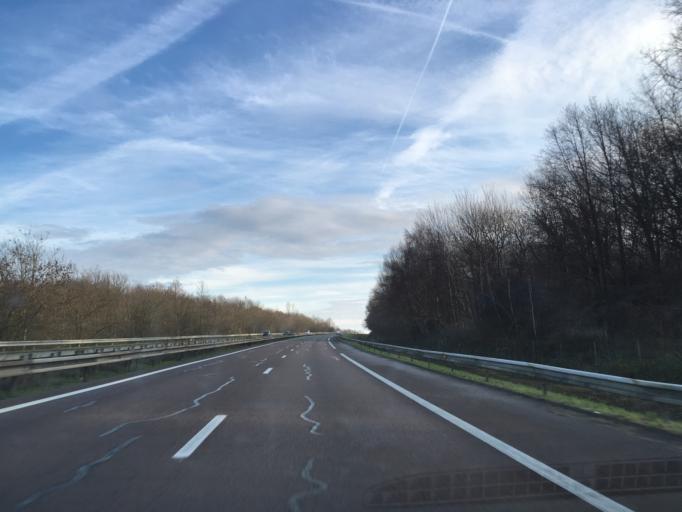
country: FR
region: Picardie
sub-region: Departement de l'Aisne
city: Charly-sur-Marne
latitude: 49.0457
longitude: 3.2631
